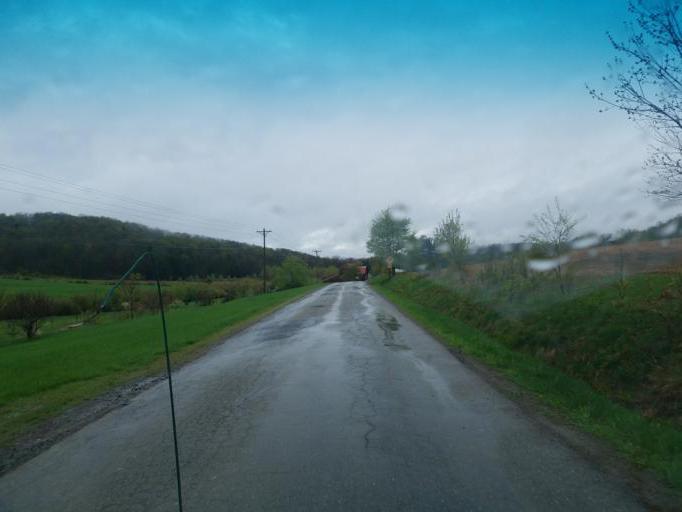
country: US
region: Pennsylvania
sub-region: Tioga County
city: Westfield
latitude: 41.9717
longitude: -77.6675
